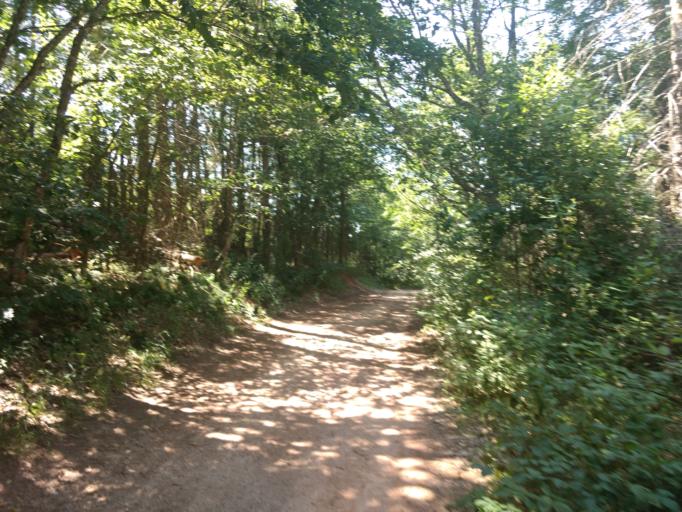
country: FR
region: Midi-Pyrenees
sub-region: Departement de l'Aveyron
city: Laissac
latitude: 44.3654
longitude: 2.7566
